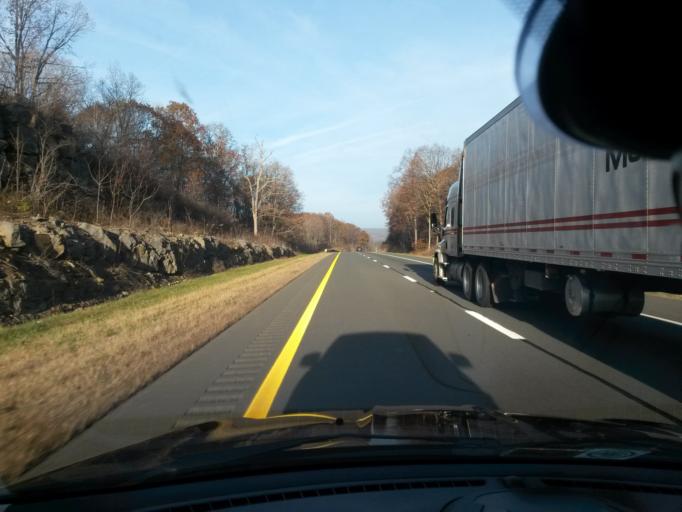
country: US
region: West Virginia
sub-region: Greenbrier County
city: Lewisburg
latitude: 37.8301
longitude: -80.4516
